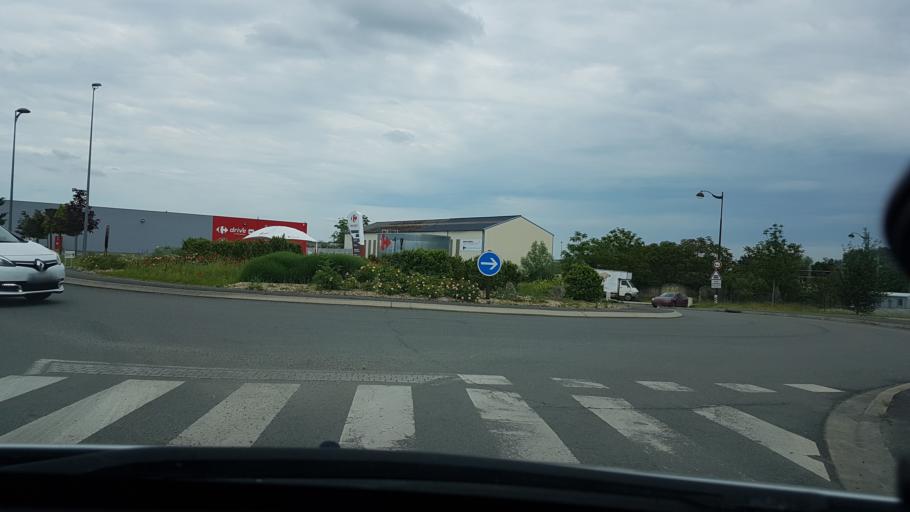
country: FR
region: Centre
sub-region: Departement du Cher
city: Bourges
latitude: 47.0951
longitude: 2.4406
